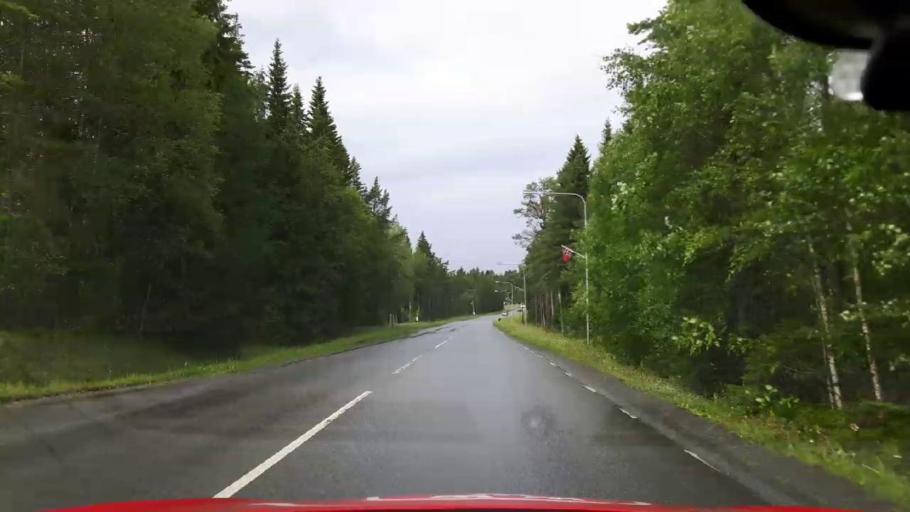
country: SE
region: Jaemtland
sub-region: Krokoms Kommun
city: Krokom
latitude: 63.3434
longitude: 14.2653
